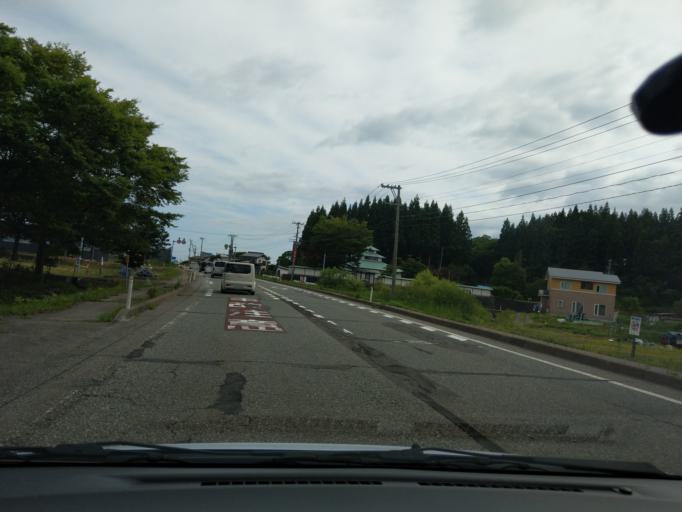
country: JP
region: Akita
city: Yokotemachi
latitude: 39.3733
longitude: 140.5693
